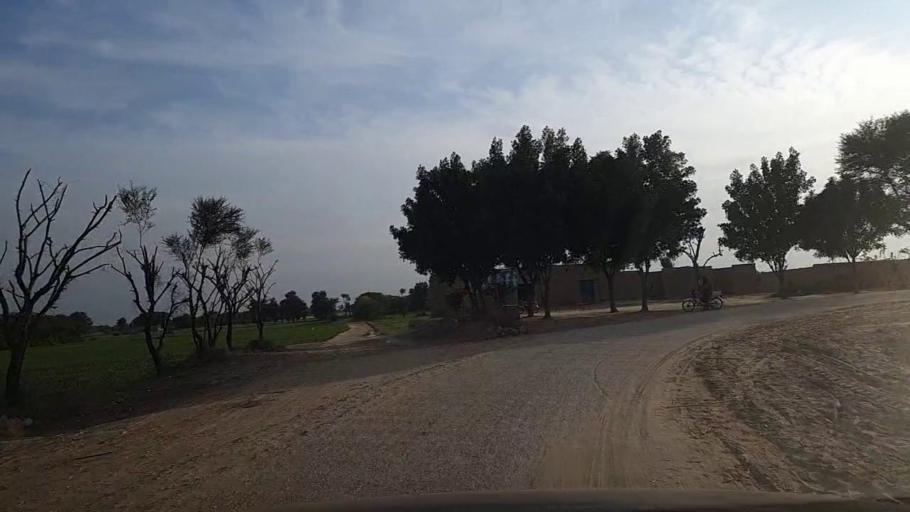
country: PK
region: Sindh
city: Jam Sahib
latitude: 26.4322
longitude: 68.5715
